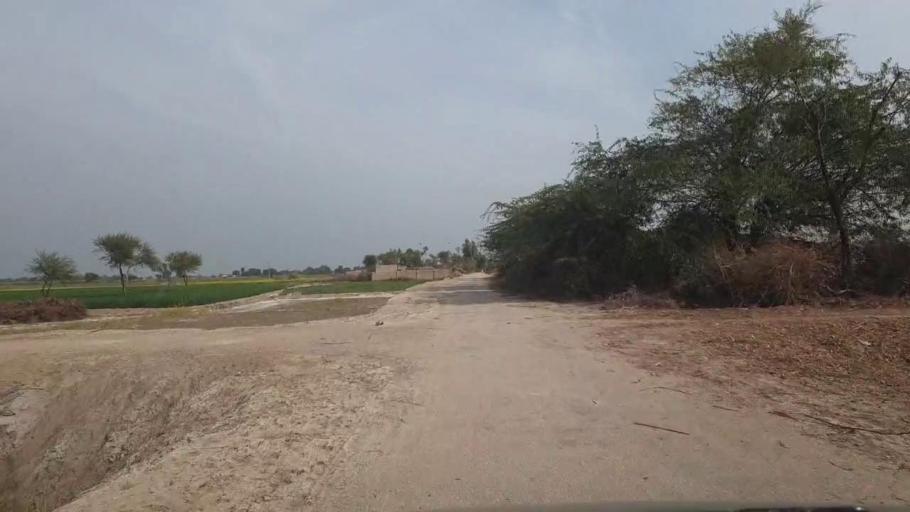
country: PK
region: Sindh
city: Shahpur Chakar
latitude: 26.0909
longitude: 68.4883
